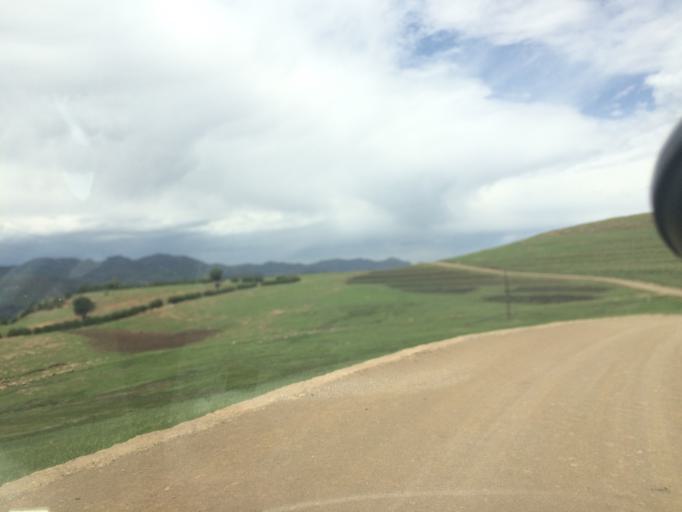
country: LS
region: Maseru
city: Nako
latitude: -29.8714
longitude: 28.0408
